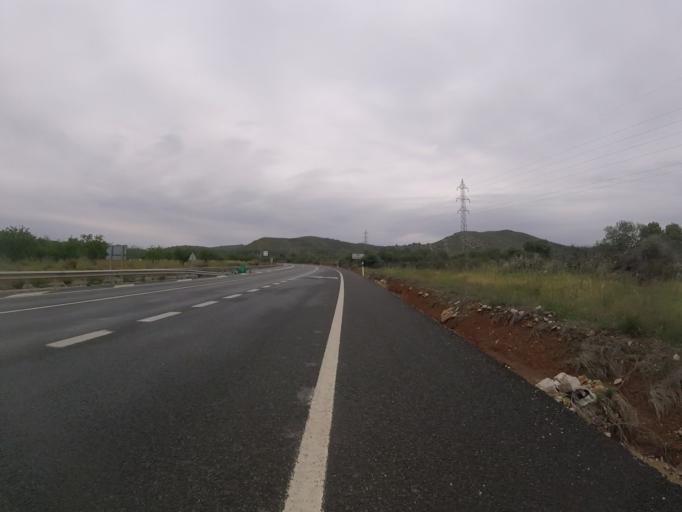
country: ES
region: Valencia
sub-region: Provincia de Castello
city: Alcala de Xivert
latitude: 40.2697
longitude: 0.2408
